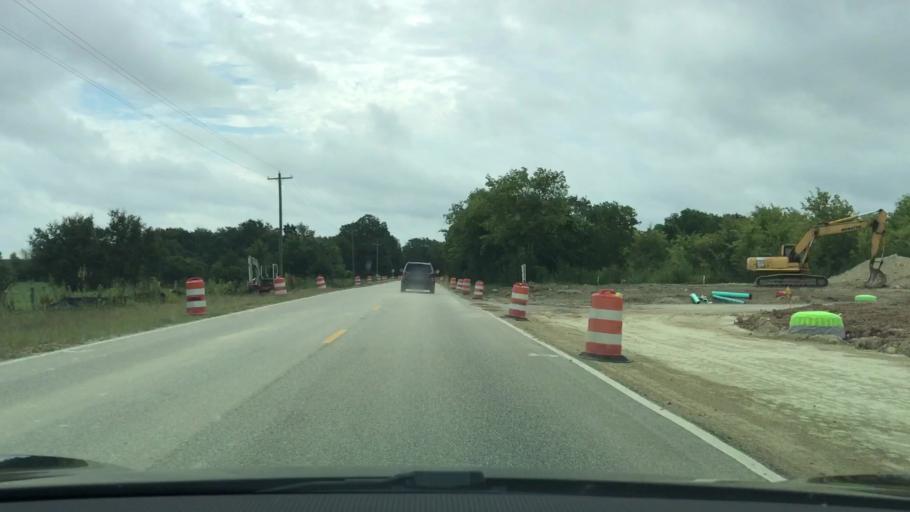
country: US
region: Alabama
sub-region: Montgomery County
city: Pike Road
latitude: 32.2872
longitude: -86.0801
